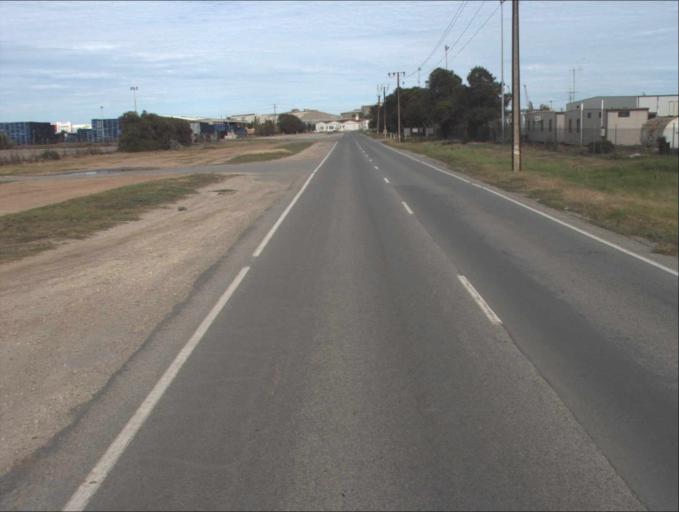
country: AU
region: South Australia
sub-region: Port Adelaide Enfield
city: Birkenhead
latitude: -34.8308
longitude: 138.5176
